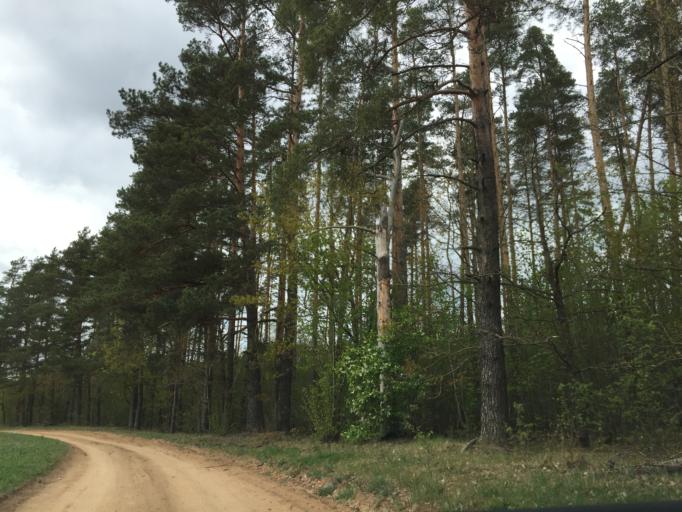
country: LV
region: Kekava
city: Kekava
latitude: 56.7998
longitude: 24.3057
